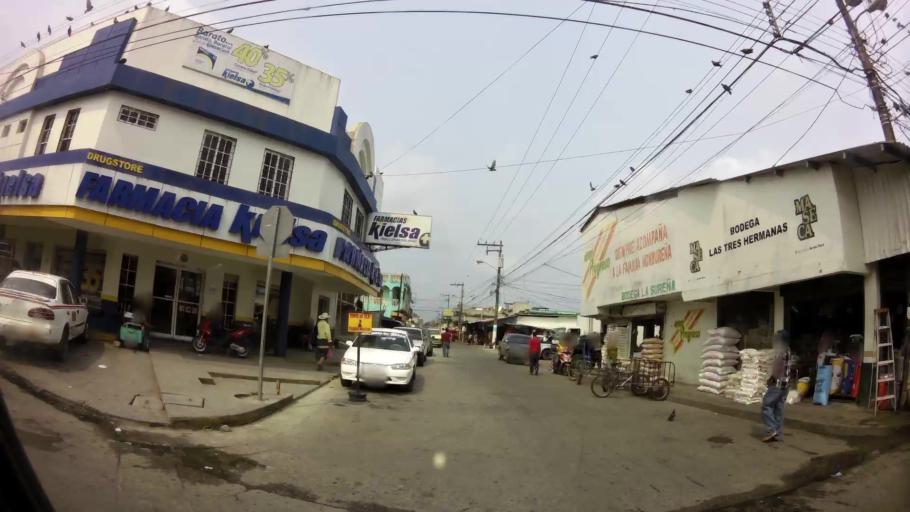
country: HN
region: Atlantida
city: Tela
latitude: 15.7846
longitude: -87.4501
